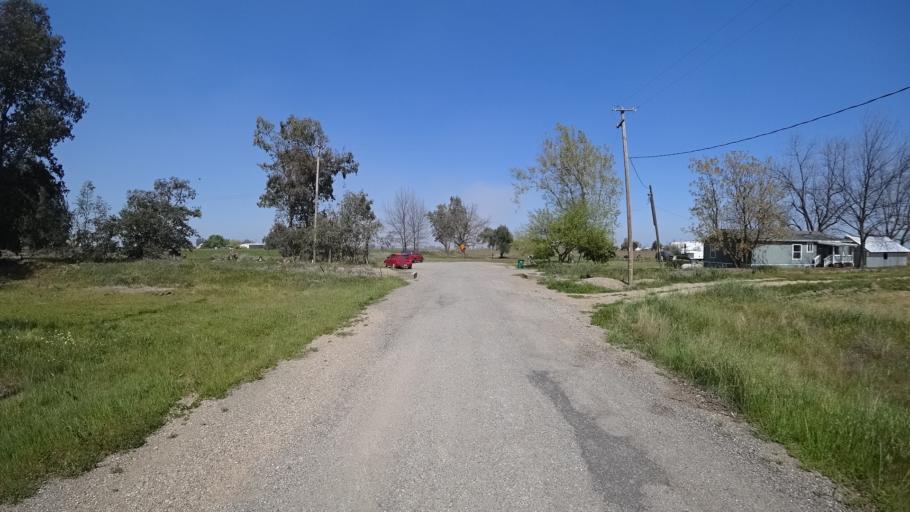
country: US
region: California
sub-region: Glenn County
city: Willows
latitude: 39.5471
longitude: -122.0981
